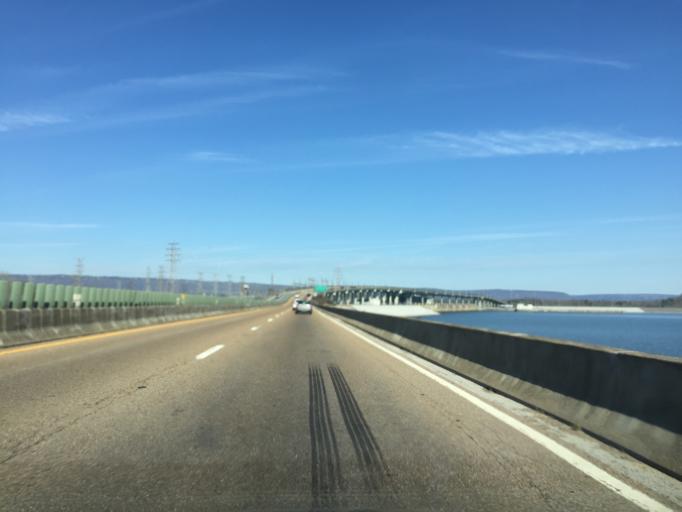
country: US
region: Tennessee
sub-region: Hamilton County
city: East Chattanooga
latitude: 35.0972
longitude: -85.2269
